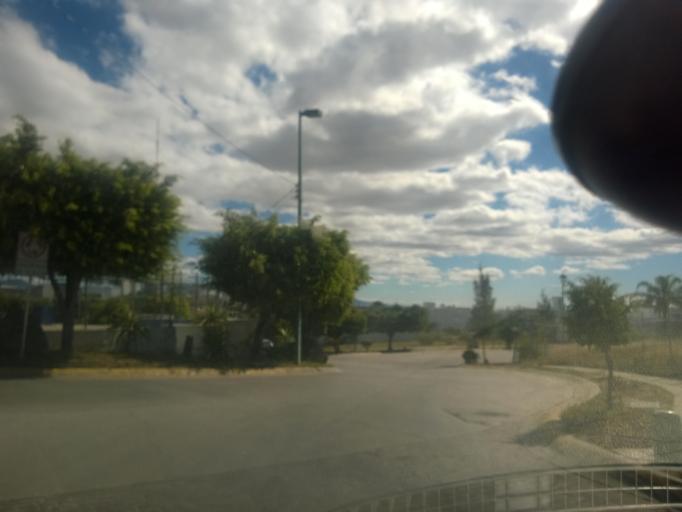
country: MX
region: Guanajuato
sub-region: Leon
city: La Ermita
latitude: 21.1528
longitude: -101.7271
